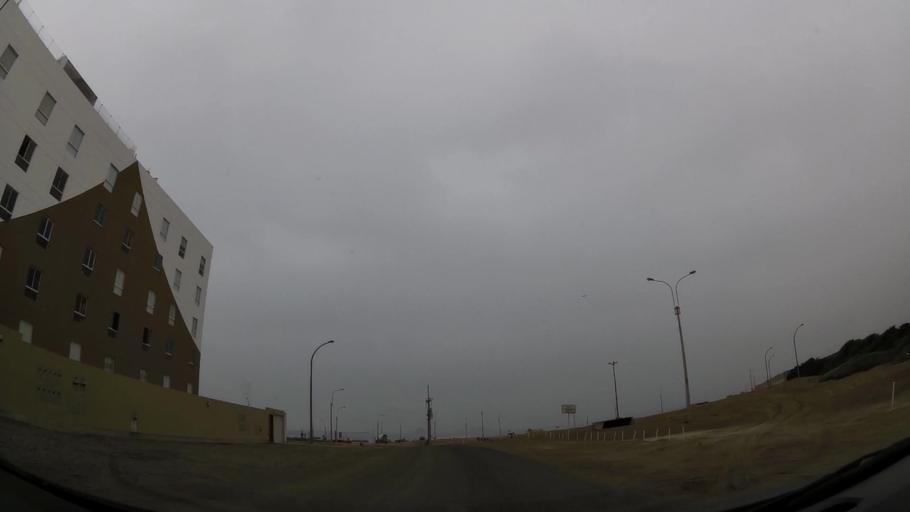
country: PE
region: Lima
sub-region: Lima
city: Punta Hermosa
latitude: -12.3236
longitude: -76.8353
